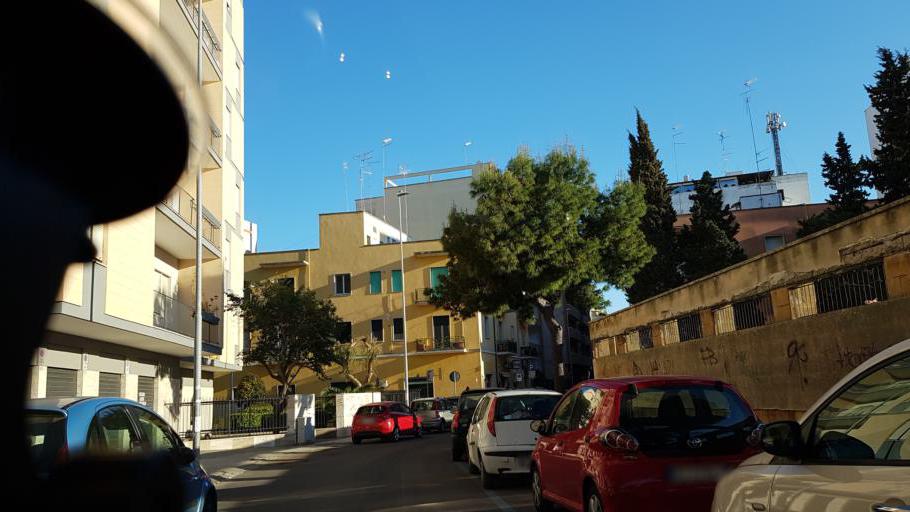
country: IT
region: Apulia
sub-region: Provincia di Lecce
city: Lecce
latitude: 40.3553
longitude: 18.1817
